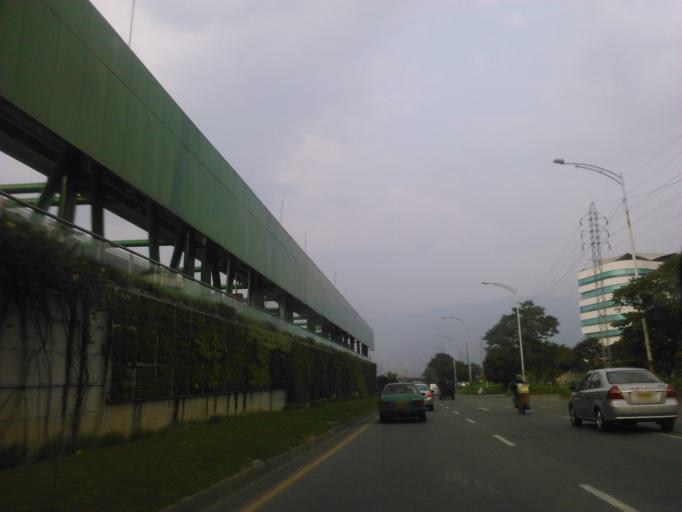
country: CO
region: Antioquia
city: Sabaneta
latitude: 6.1575
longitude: -75.6163
